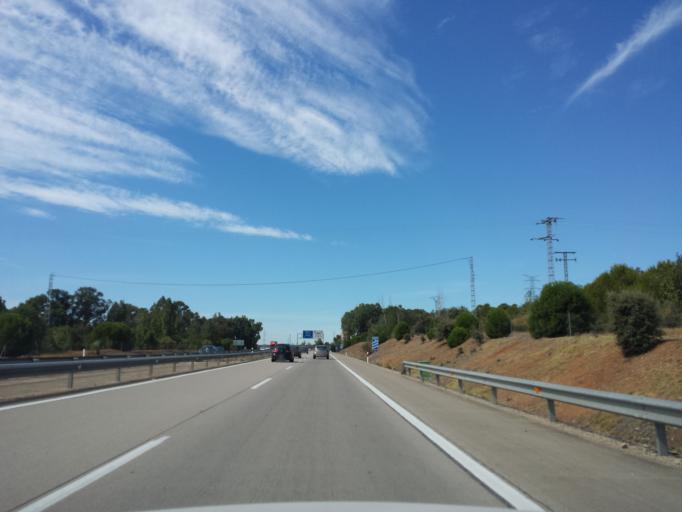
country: ES
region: Castille-La Mancha
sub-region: Province of Toledo
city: Talavera de la Reina
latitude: 39.9875
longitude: -4.8431
